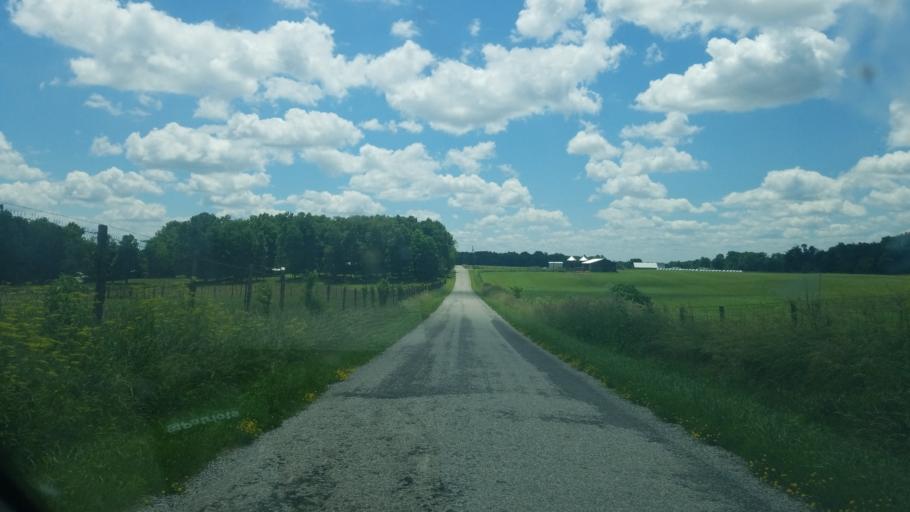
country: US
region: Ohio
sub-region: Ashland County
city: Ashland
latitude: 40.9887
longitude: -82.3268
